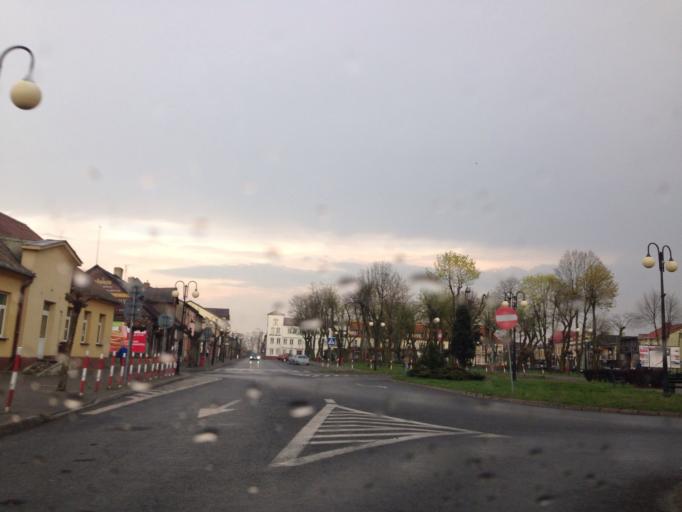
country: PL
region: Masovian Voivodeship
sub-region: Powiat plonski
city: Raciaz
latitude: 52.7816
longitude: 20.1170
